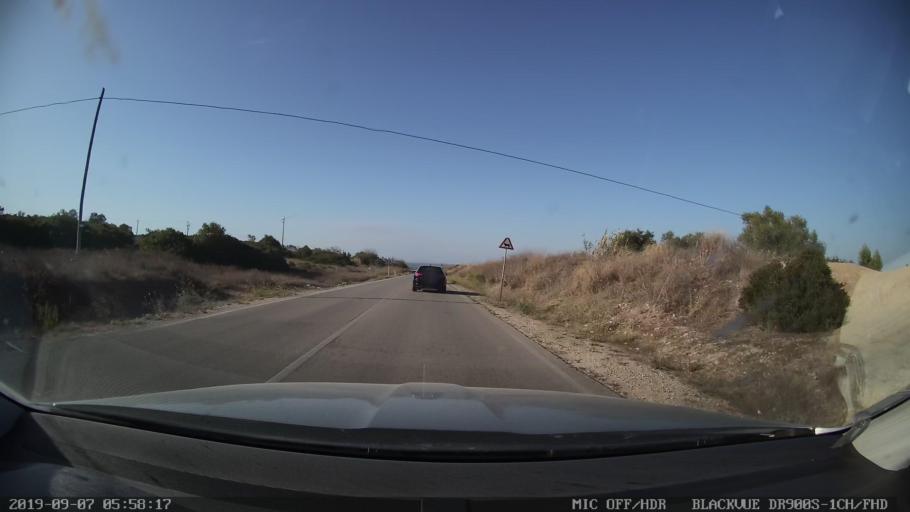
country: PT
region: Setubal
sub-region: Sesimbra
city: Sesimbra
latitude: 38.4580
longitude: -9.0938
